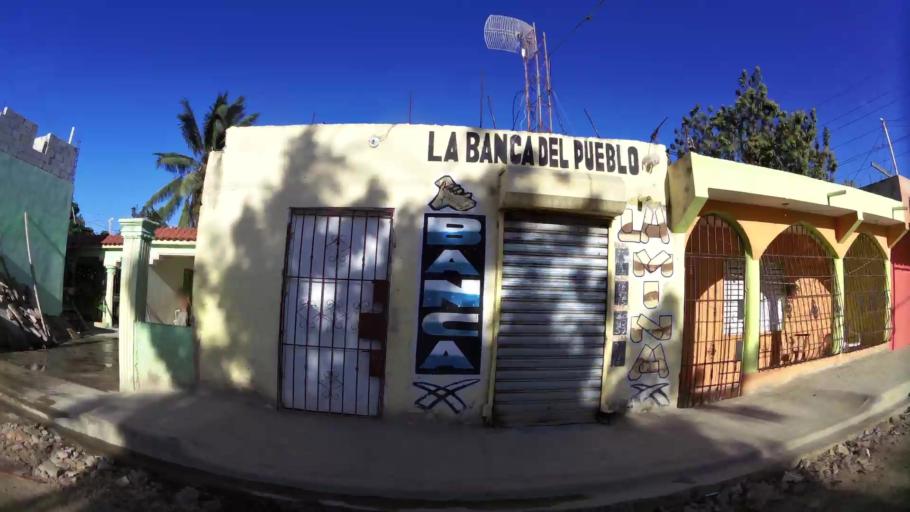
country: DO
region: Santo Domingo
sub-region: Santo Domingo
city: Santo Domingo Este
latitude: 18.4769
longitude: -69.8153
